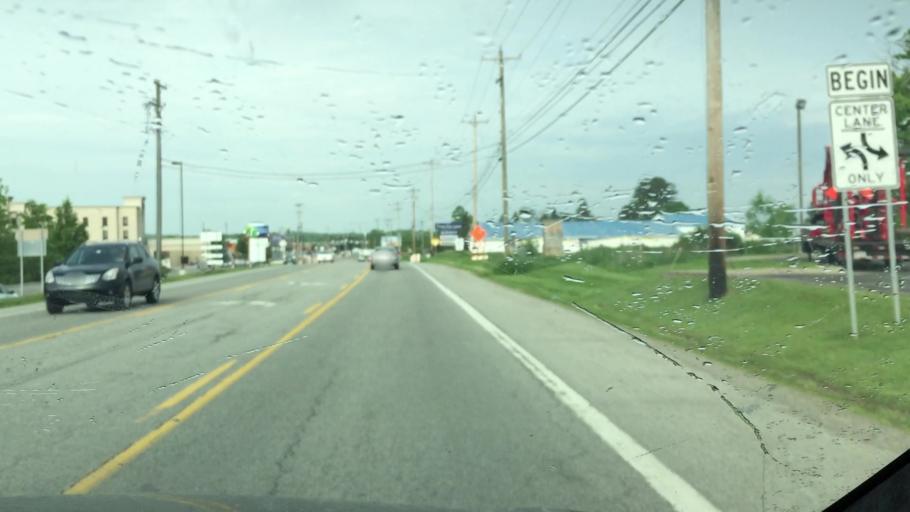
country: US
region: Pennsylvania
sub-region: Mercer County
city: Grove City
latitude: 41.1418
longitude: -80.1668
